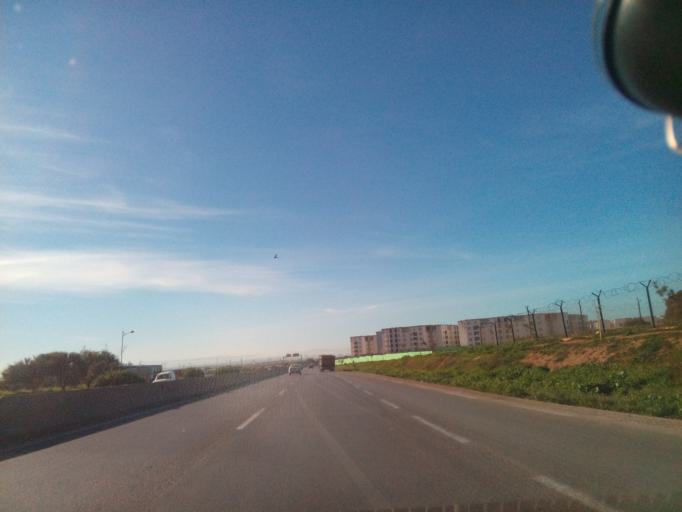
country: DZ
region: Oran
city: Ain el Bya
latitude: 35.7837
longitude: -0.4121
